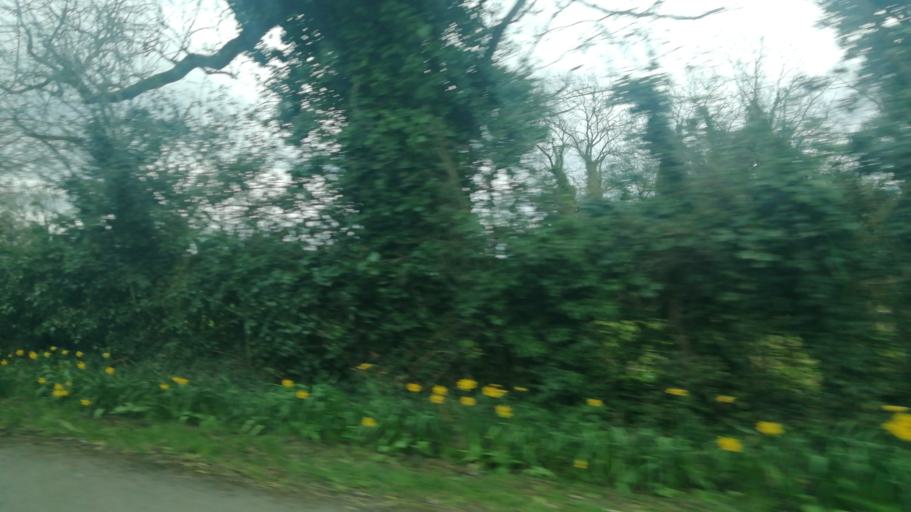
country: IE
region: Leinster
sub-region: Kildare
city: Prosperous
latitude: 53.2931
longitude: -6.7490
